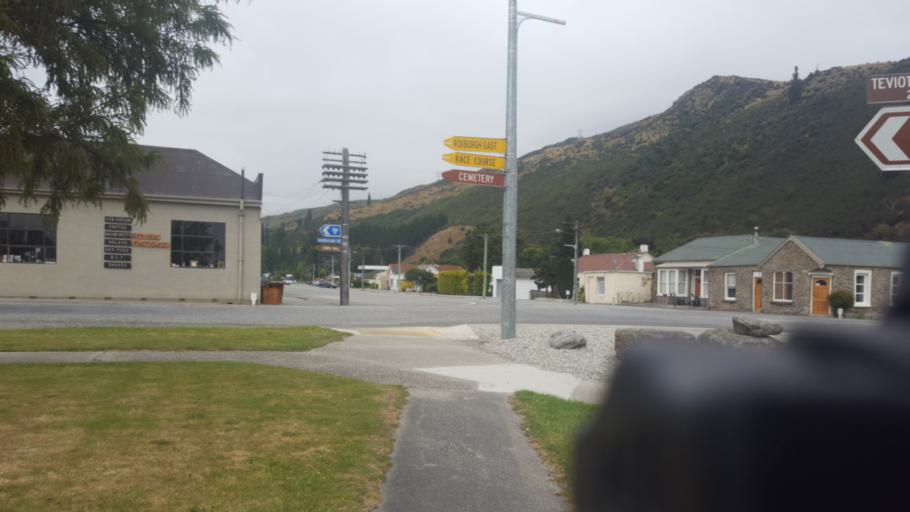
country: NZ
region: Otago
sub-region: Queenstown-Lakes District
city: Kingston
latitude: -45.5418
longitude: 169.3156
